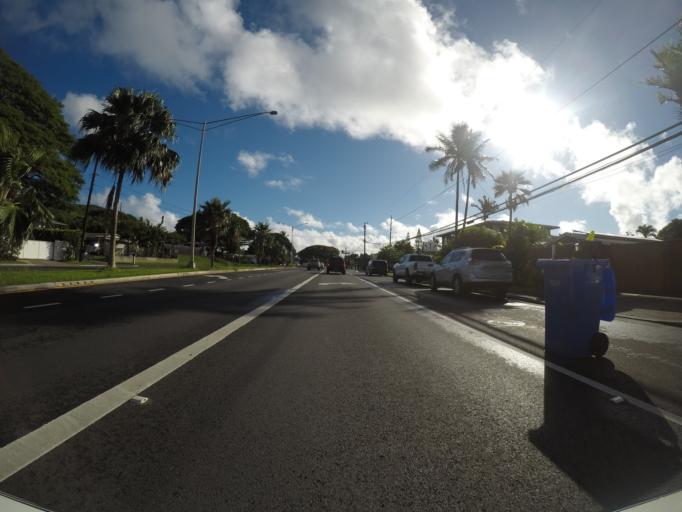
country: US
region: Hawaii
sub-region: Honolulu County
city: Kailua
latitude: 21.4090
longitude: -157.7555
